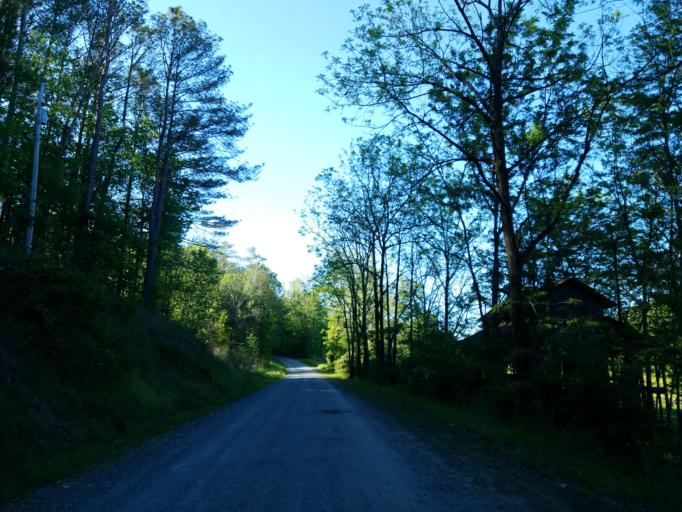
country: US
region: Georgia
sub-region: Gilmer County
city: Ellijay
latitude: 34.5930
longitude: -84.5112
